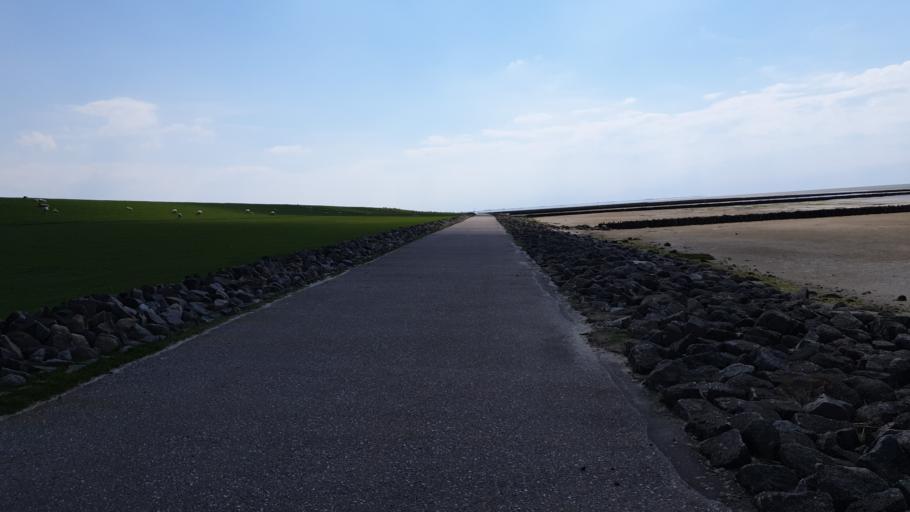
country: DE
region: Schleswig-Holstein
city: Elisabeth-Sophien-Koog
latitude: 54.4781
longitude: 8.8112
